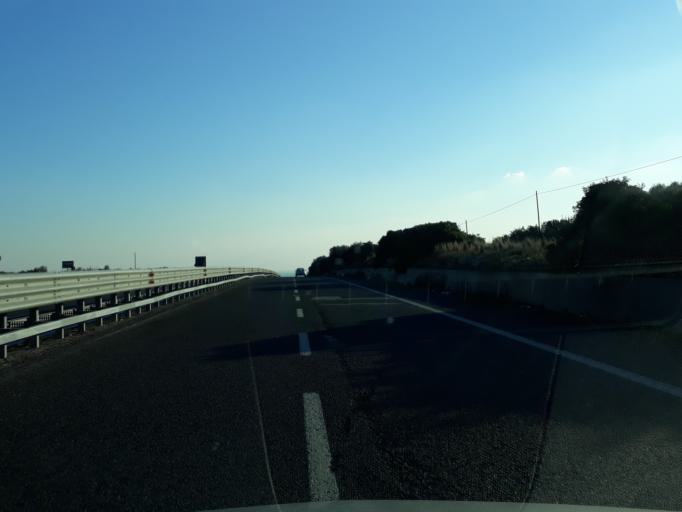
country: IT
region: Apulia
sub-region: Provincia di Taranto
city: Montemesola
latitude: 40.5784
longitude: 17.2869
